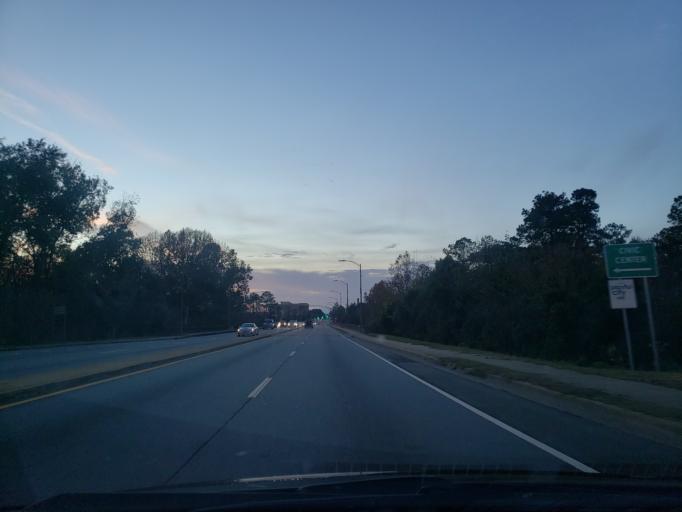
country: US
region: Georgia
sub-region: Dougherty County
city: Albany
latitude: 31.5756
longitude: -84.1456
